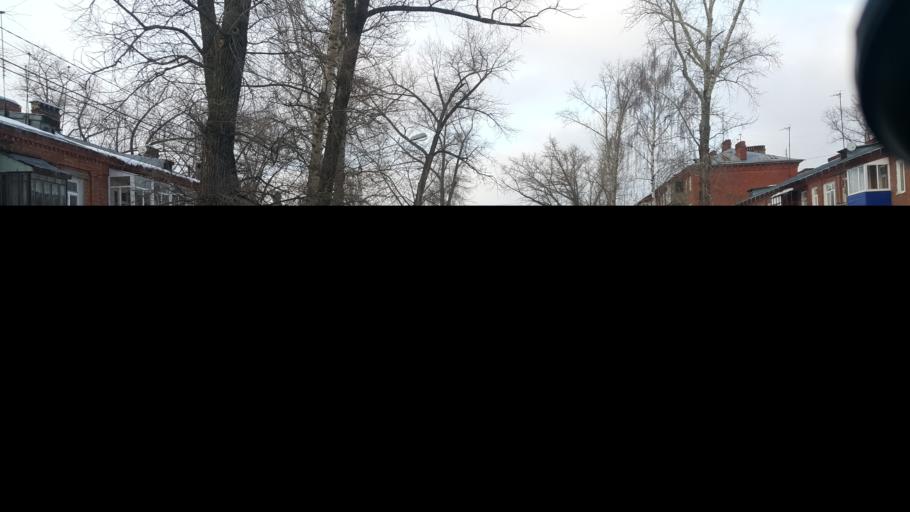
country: RU
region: Tambov
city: Kotovsk
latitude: 52.5968
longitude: 41.4954
